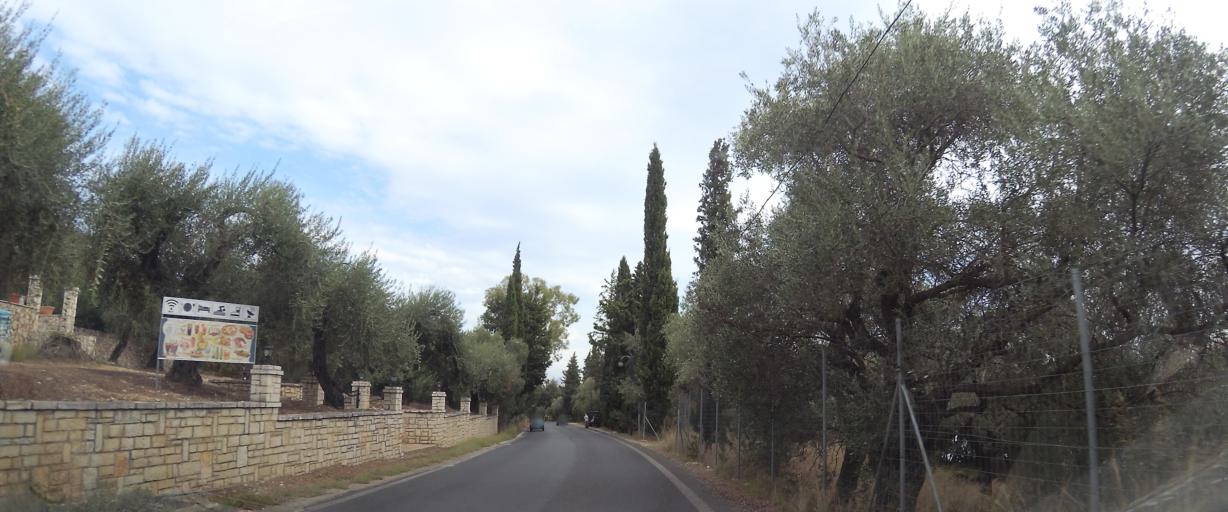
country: GR
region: Ionian Islands
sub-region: Nomos Kerkyras
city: Kontokali
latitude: 39.7242
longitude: 19.8856
